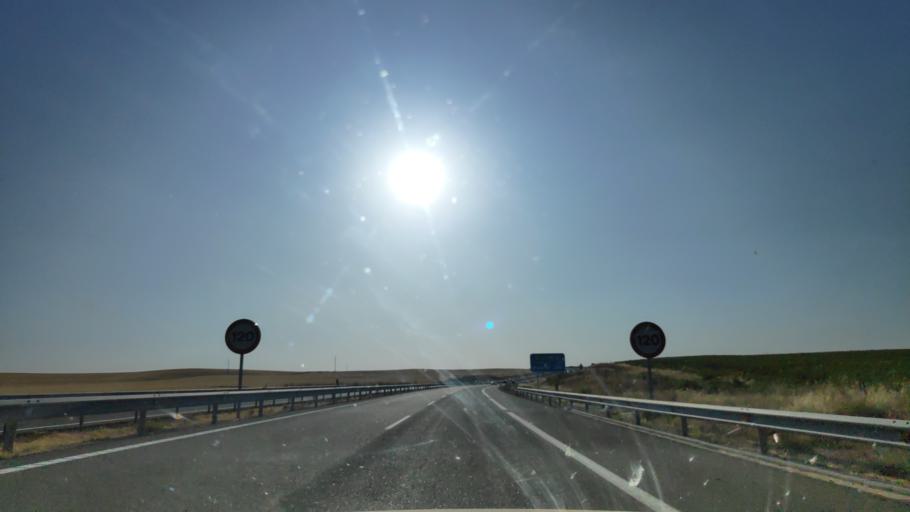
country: ES
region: Castille-La Mancha
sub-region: Provincia de Cuenca
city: Montalbo
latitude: 39.8736
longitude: -2.6191
